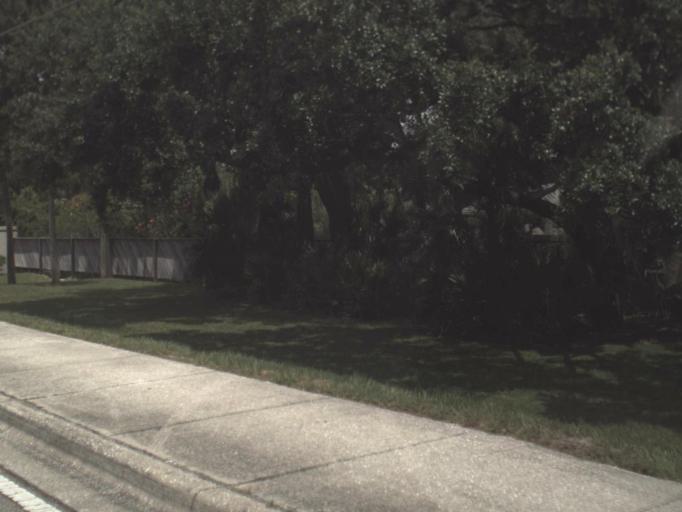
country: US
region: Florida
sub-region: Pinellas County
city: Oldsmar
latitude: 28.0477
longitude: -82.6898
